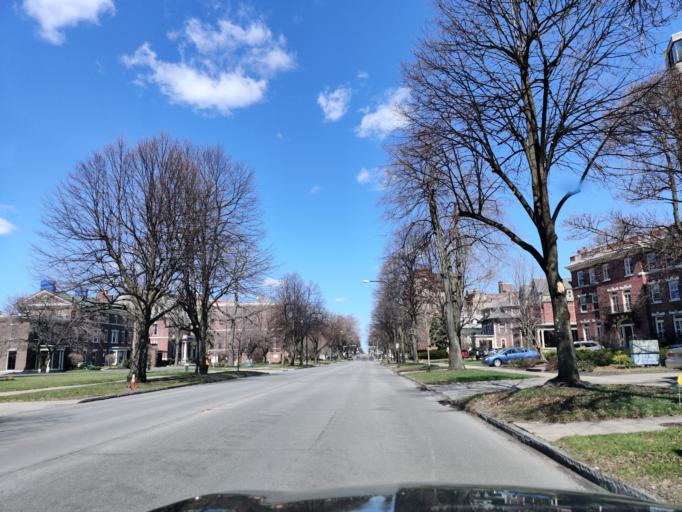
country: US
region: New York
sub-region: Erie County
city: Buffalo
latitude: 42.9069
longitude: -78.8716
